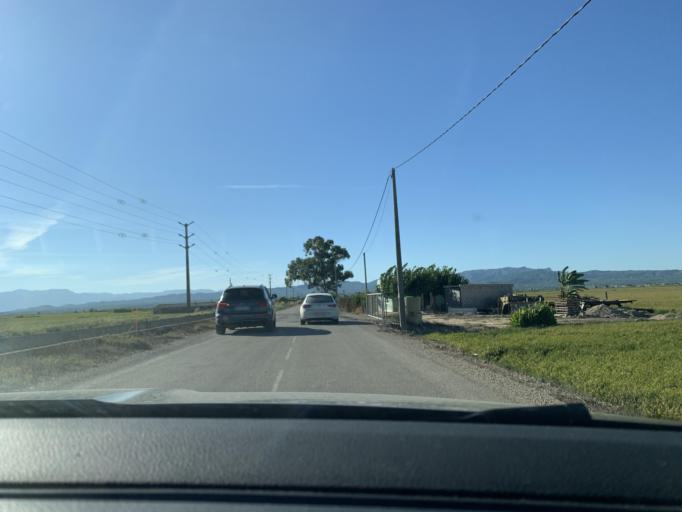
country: ES
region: Catalonia
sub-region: Provincia de Tarragona
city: Deltebre
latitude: 40.7513
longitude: 0.7227
